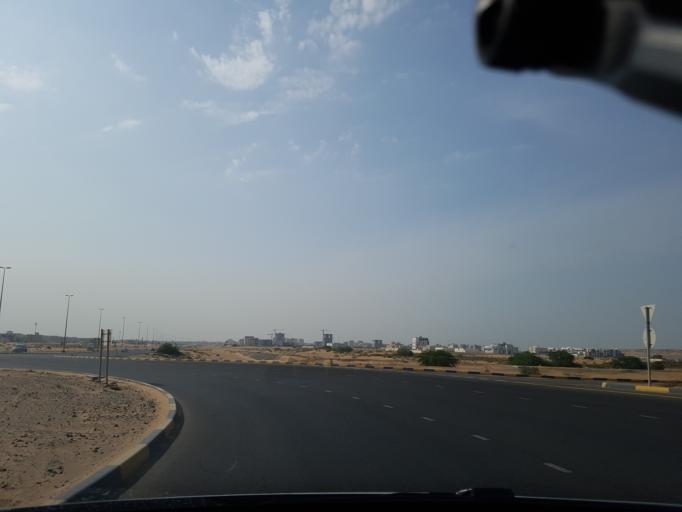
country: AE
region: Ajman
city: Ajman
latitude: 25.4140
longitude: 55.5569
